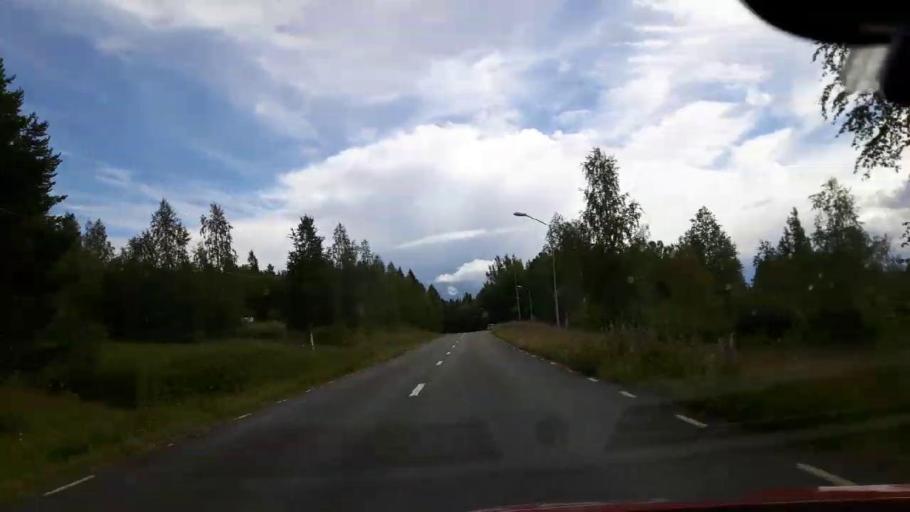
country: SE
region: Jaemtland
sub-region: Stroemsunds Kommun
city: Stroemsund
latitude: 64.3392
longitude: 14.9532
